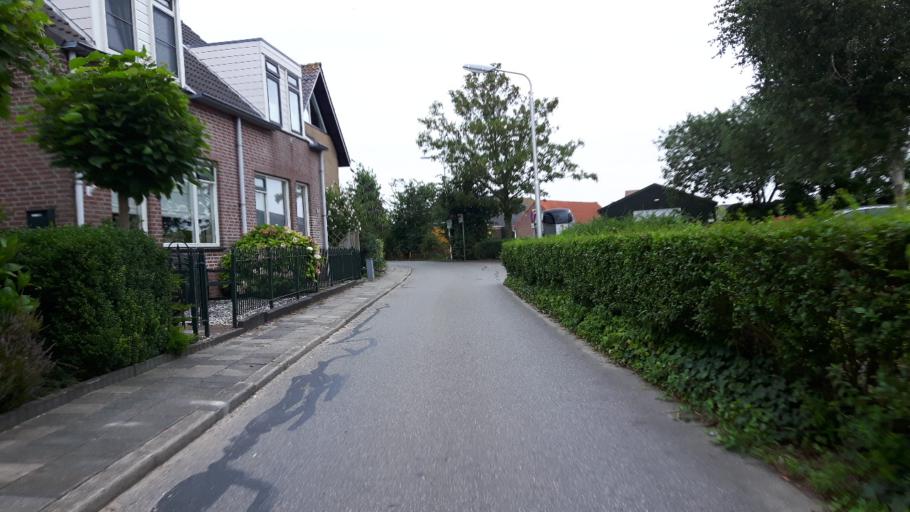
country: NL
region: South Holland
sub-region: Gemeente Kaag en Braassem
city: Oude Wetering
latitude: 52.1846
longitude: 4.6309
